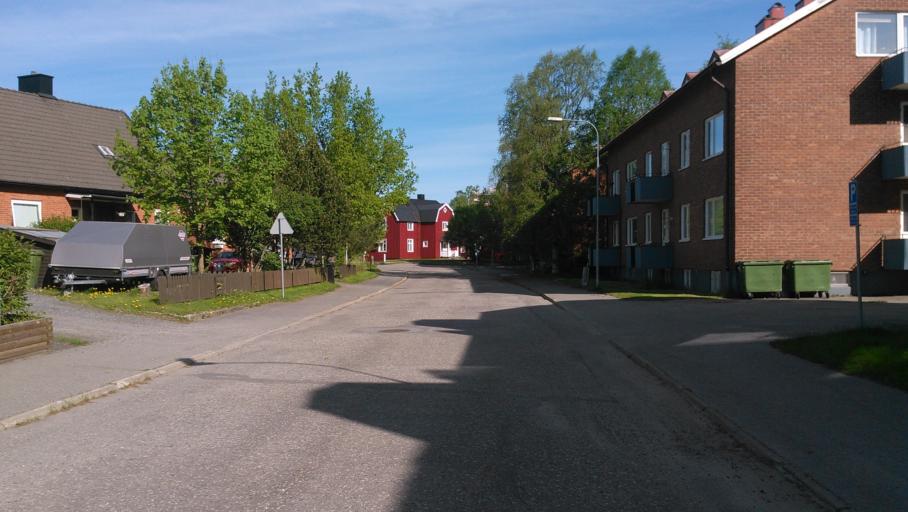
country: SE
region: Vaesterbotten
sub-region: Umea Kommun
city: Umea
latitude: 63.8109
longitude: 20.3018
